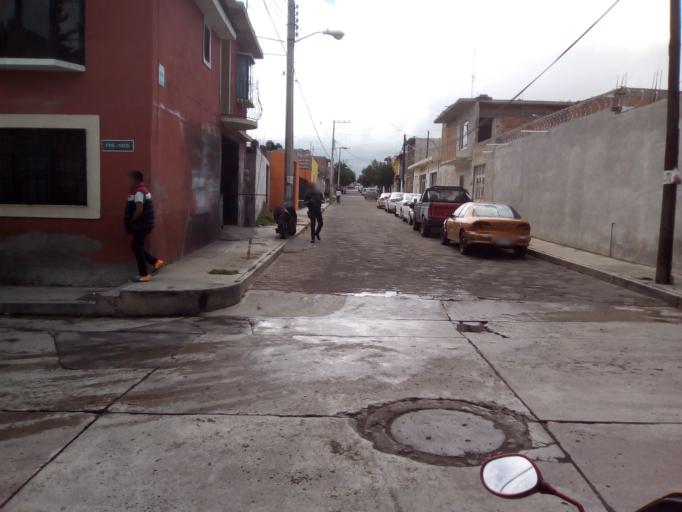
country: MX
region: Guerrero
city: San Luis de la Paz
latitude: 21.2917
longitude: -100.5115
